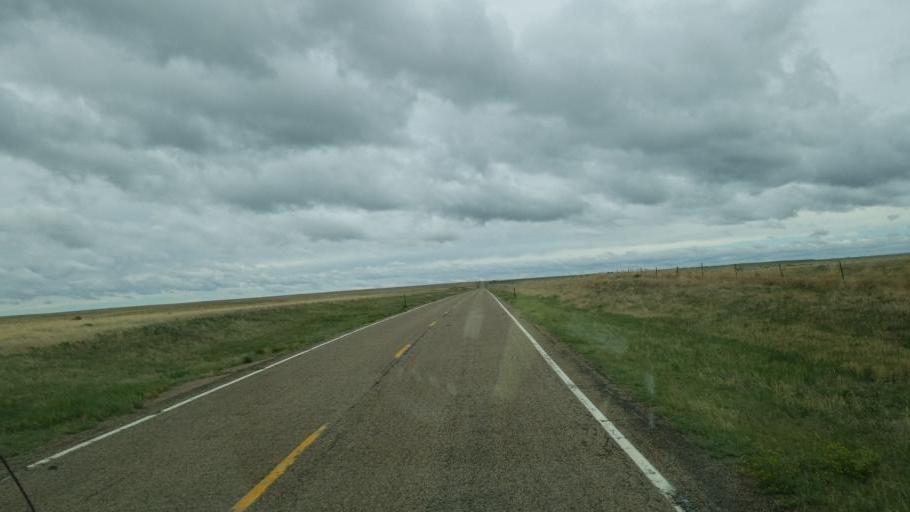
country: US
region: Colorado
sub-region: Lincoln County
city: Hugo
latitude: 38.8509
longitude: -103.6073
